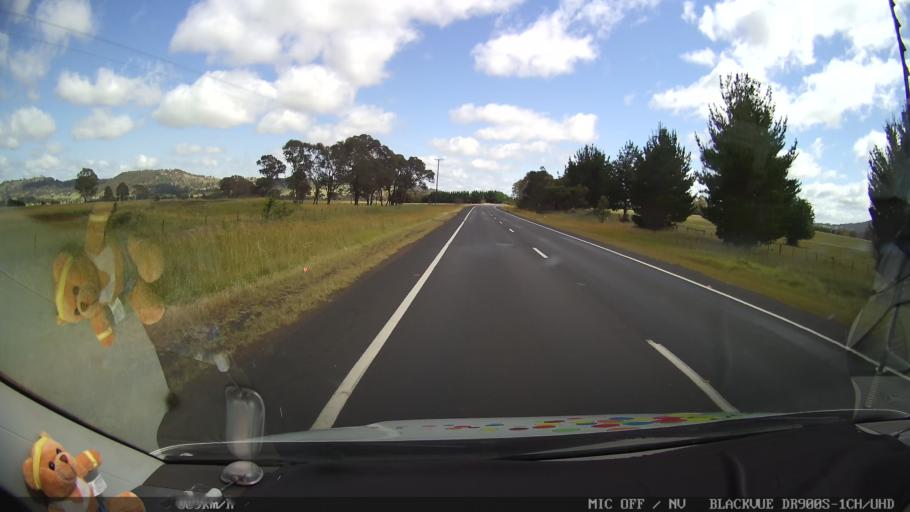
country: AU
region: New South Wales
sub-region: Glen Innes Severn
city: Glen Innes
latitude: -29.8808
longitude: 151.7341
